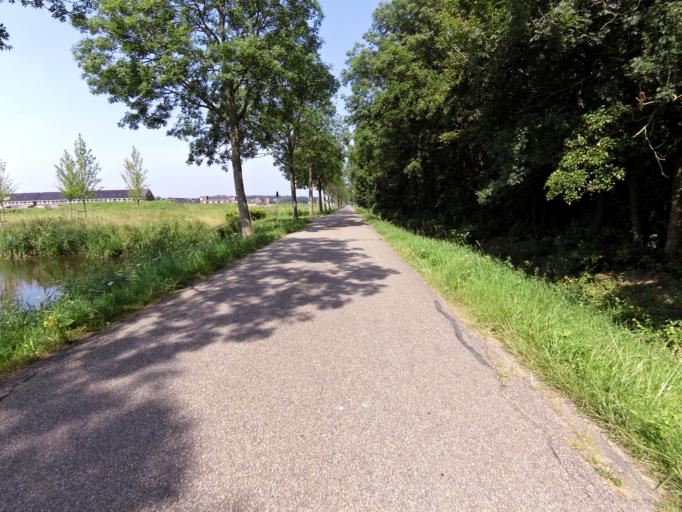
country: NL
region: South Holland
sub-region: Gemeente Dordrecht
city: Dordrecht
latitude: 51.7685
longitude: 4.6624
